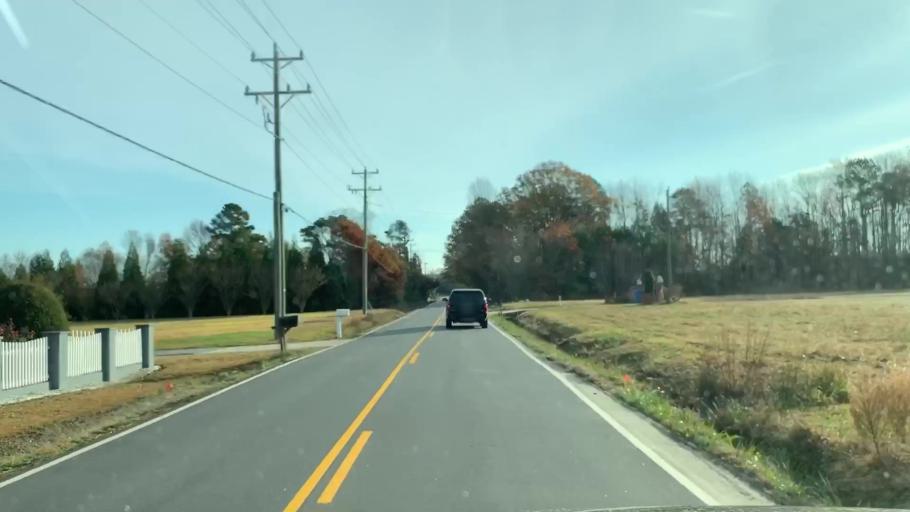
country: US
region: Virginia
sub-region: City of Virginia Beach
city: Virginia Beach
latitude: 36.6907
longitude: -76.0301
